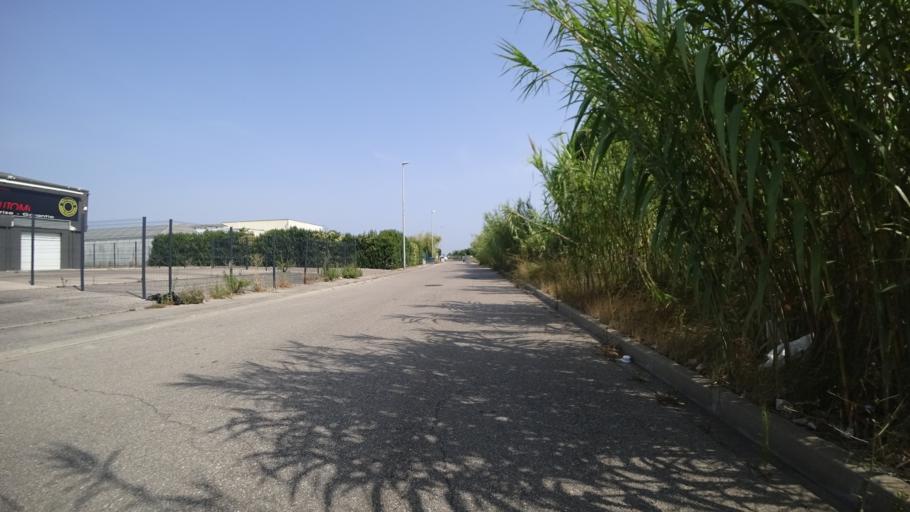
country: FR
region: Languedoc-Roussillon
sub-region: Departement des Pyrenees-Orientales
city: Le Barcares
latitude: 42.7725
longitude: 3.0167
